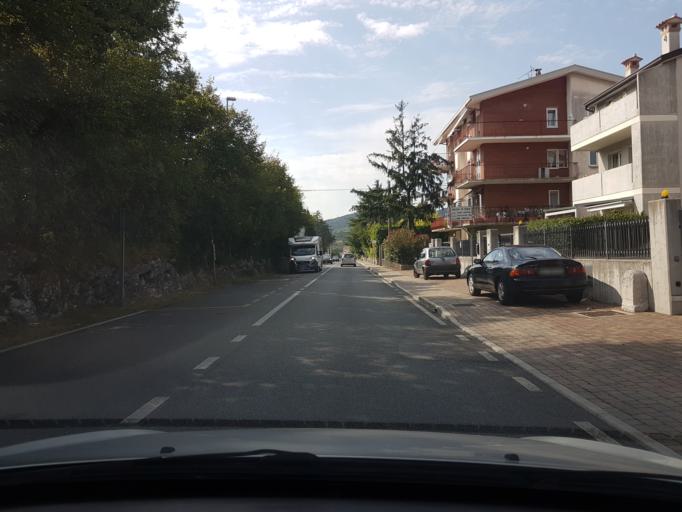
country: IT
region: Friuli Venezia Giulia
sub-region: Provincia di Trieste
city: Sistiana-Visogliano
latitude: 45.7681
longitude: 13.6424
